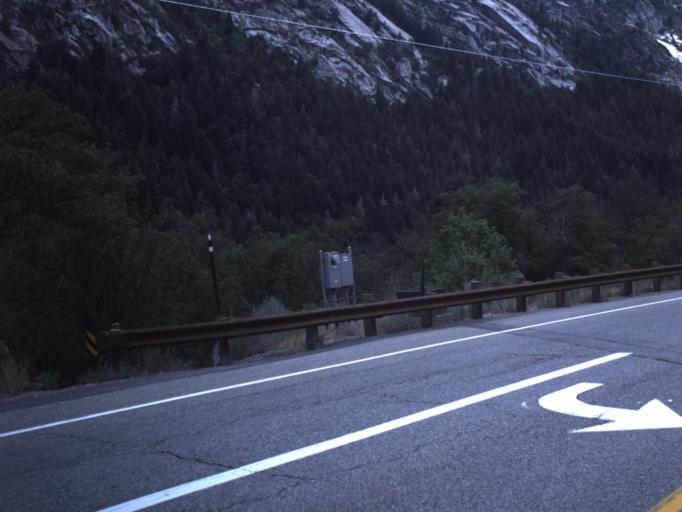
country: US
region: Utah
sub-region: Salt Lake County
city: Granite
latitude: 40.5719
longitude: -111.7587
